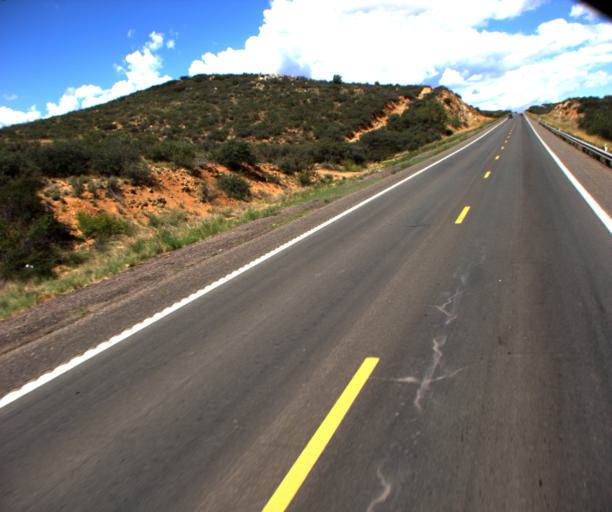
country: US
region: Arizona
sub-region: Yavapai County
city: Dewey-Humboldt
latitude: 34.5312
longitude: -112.1167
